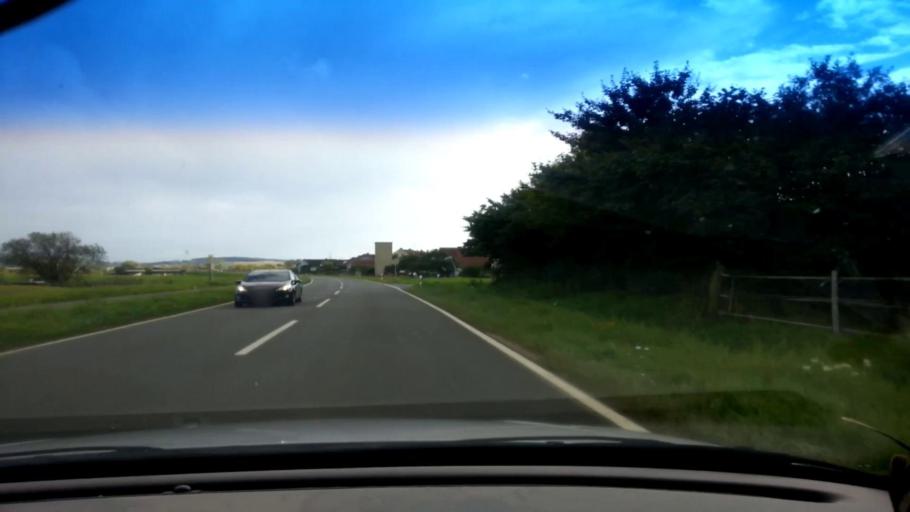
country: DE
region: Bavaria
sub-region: Upper Franconia
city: Ebensfeld
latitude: 50.0686
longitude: 10.9421
